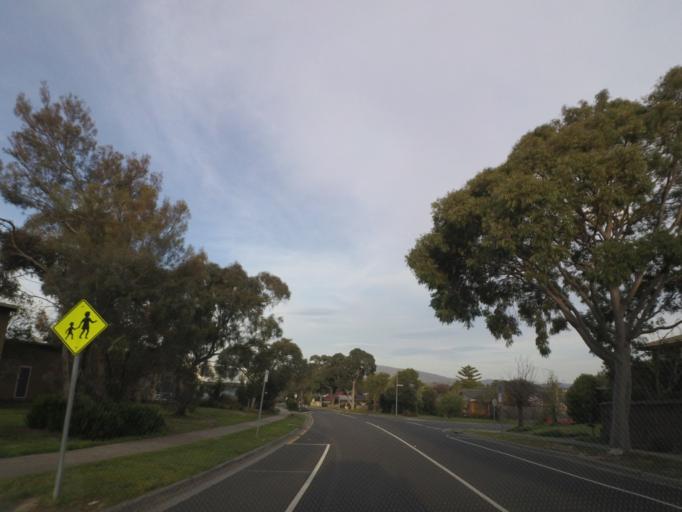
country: AU
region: Victoria
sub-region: Knox
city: Wantirna
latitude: -37.8576
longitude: 145.2295
